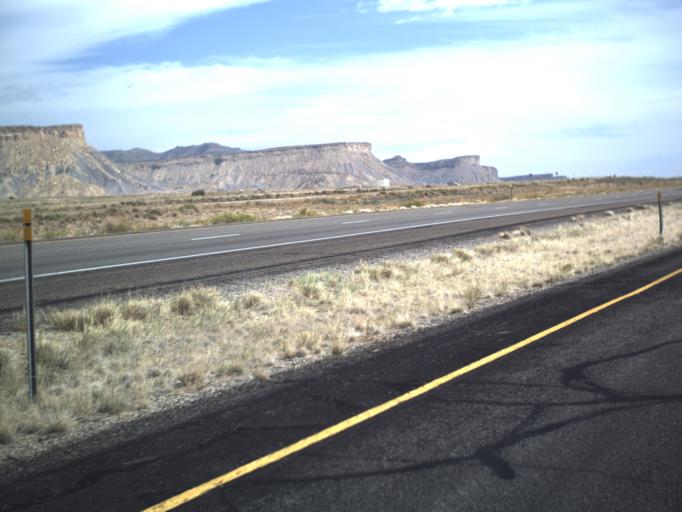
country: US
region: Utah
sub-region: Grand County
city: Moab
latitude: 38.9536
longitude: -109.7584
